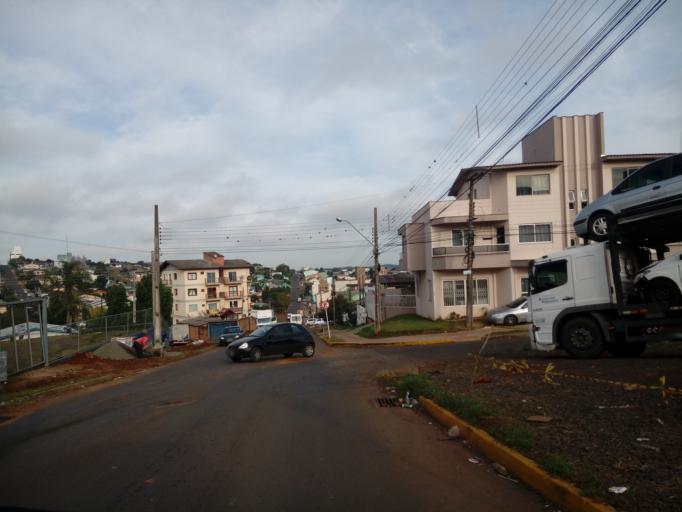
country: BR
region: Santa Catarina
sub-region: Chapeco
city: Chapeco
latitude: -27.0715
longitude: -52.6283
